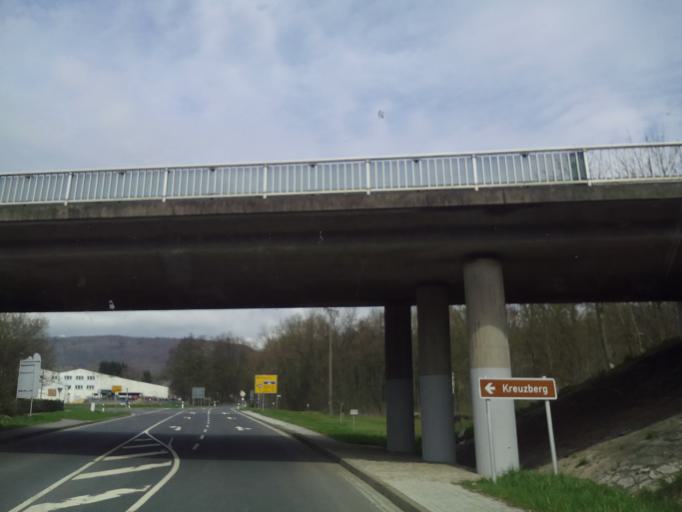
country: DE
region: Bavaria
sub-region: Regierungsbezirk Unterfranken
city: Bischofsheim an der Rhon
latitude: 50.4105
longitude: 10.0134
